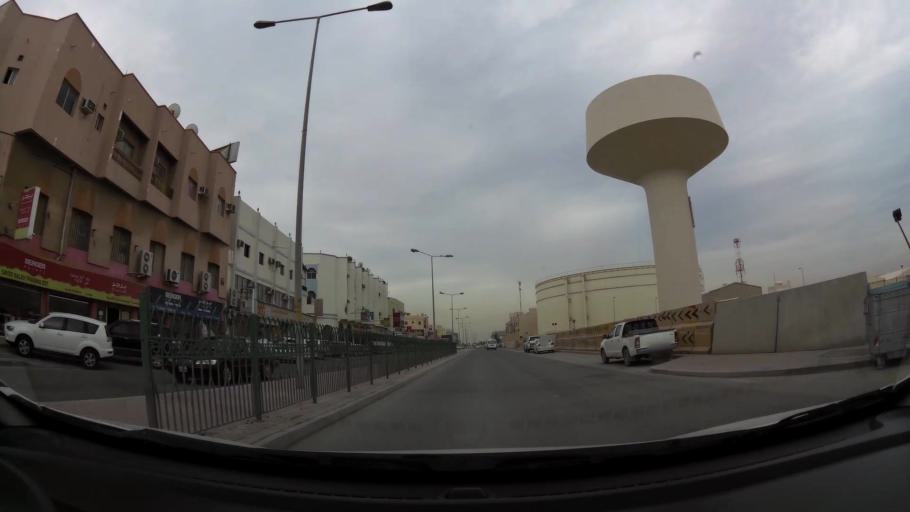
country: BH
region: Northern
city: Sitrah
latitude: 26.1653
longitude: 50.6111
